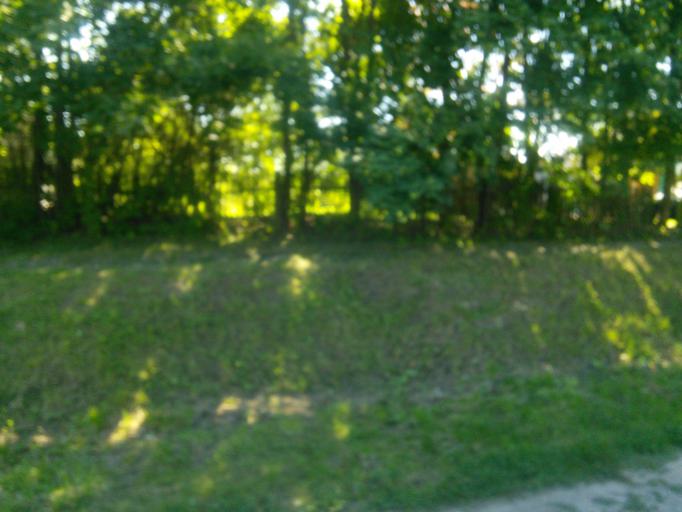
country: RU
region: Tverskaya
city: Kesova Gora
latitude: 57.5805
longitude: 37.2894
